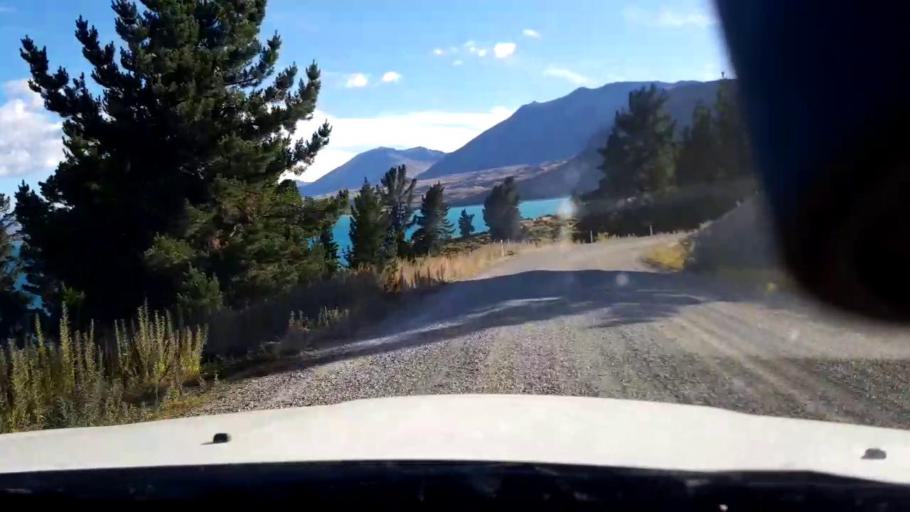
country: NZ
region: Canterbury
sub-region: Timaru District
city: Pleasant Point
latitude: -43.9644
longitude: 170.5228
